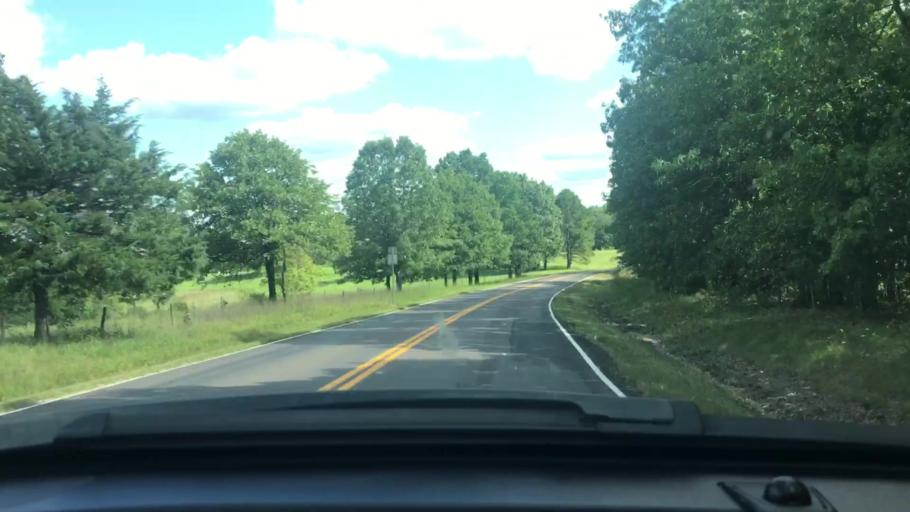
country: US
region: Missouri
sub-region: Wright County
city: Hartville
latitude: 37.3770
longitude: -92.3563
